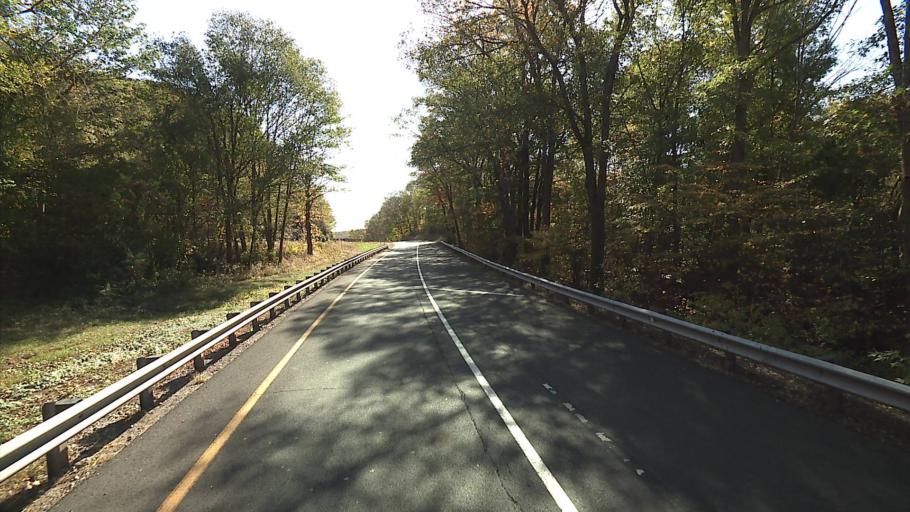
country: US
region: Connecticut
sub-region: Tolland County
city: Rockville
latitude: 41.7887
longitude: -72.4434
